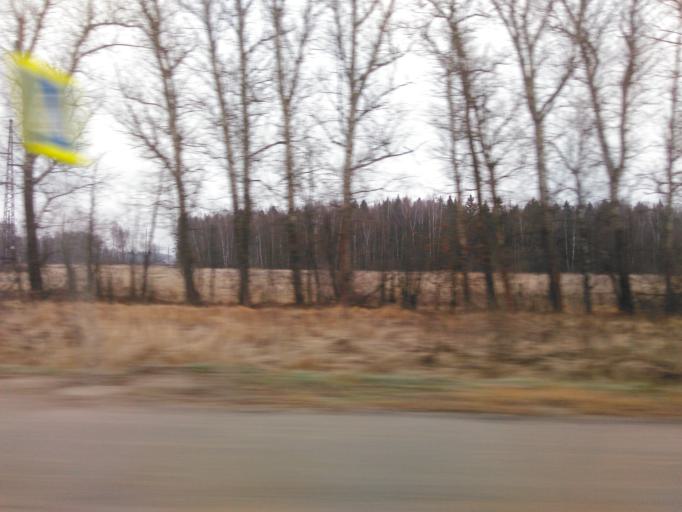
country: RU
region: Moskovskaya
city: Ashukino
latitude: 56.1321
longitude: 37.9774
